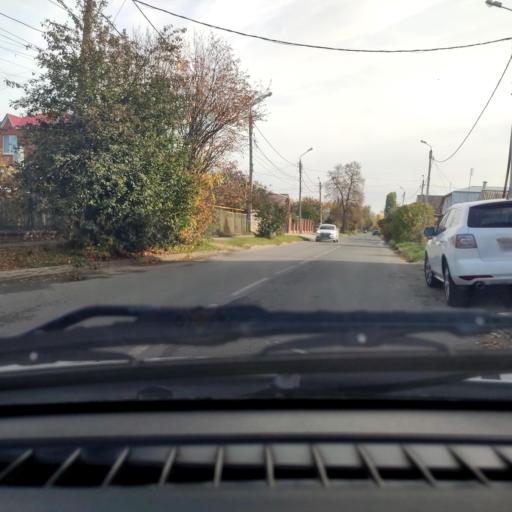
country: RU
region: Samara
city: Tol'yatti
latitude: 53.5256
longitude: 49.4146
